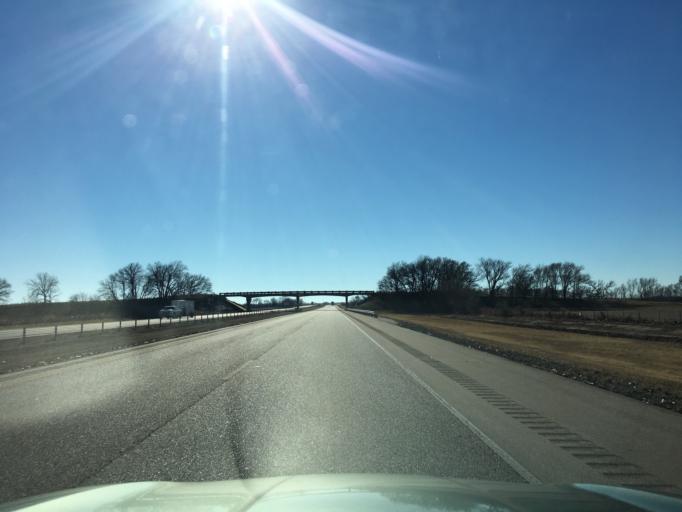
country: US
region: Oklahoma
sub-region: Kay County
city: Blackwell
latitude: 36.9147
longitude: -97.3517
